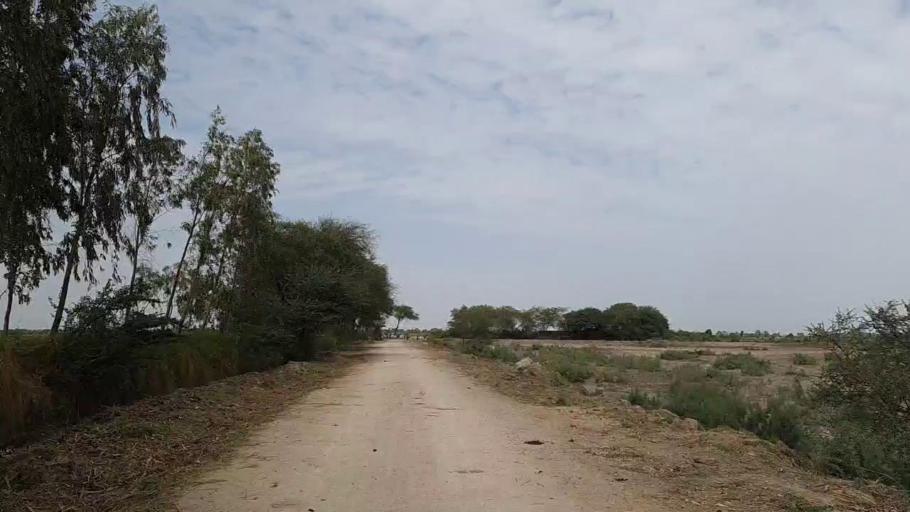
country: PK
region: Sindh
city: Daro Mehar
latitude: 24.7845
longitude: 68.2057
